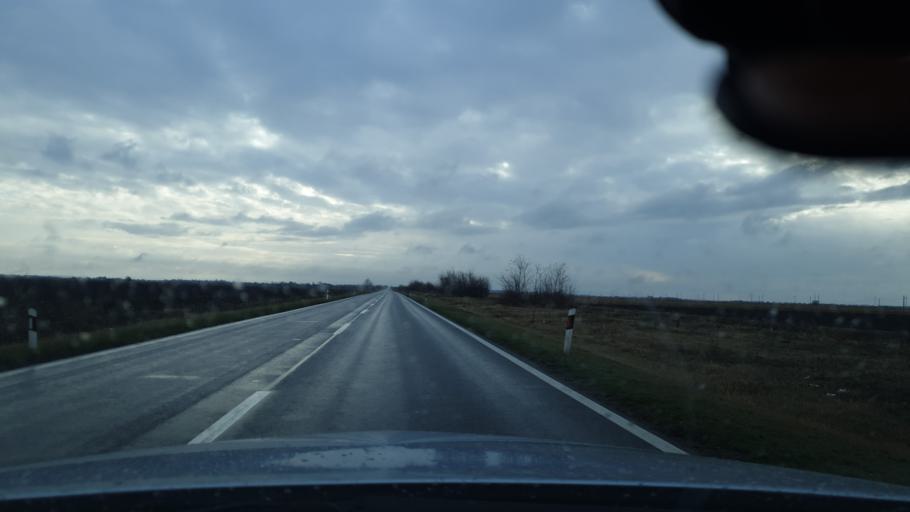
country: RS
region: Autonomna Pokrajina Vojvodina
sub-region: Juznobanatski Okrug
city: Kovin
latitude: 44.7825
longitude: 20.9281
